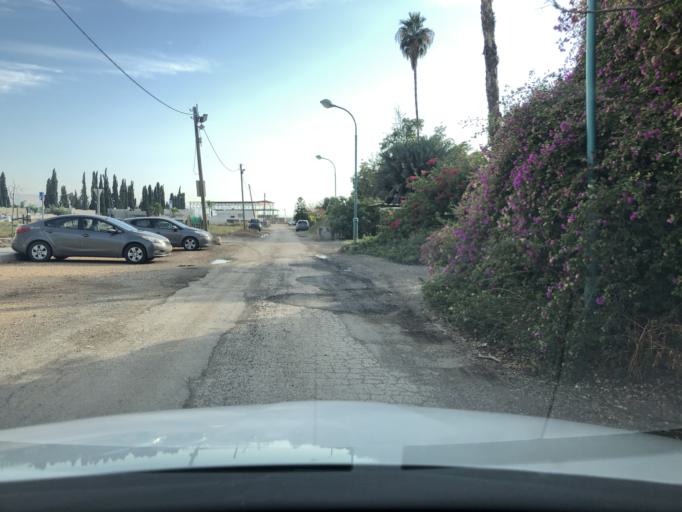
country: IL
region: Northern District
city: Yavne'el
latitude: 32.6615
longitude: 35.5852
